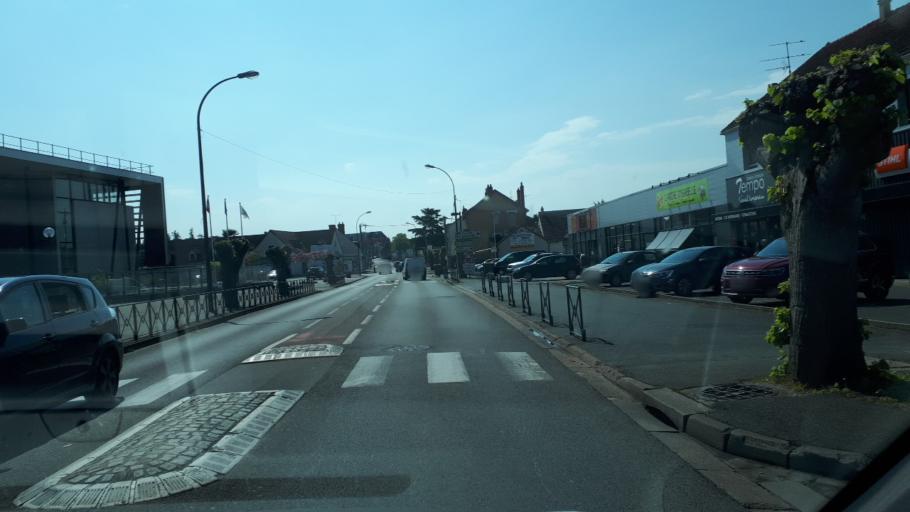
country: FR
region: Centre
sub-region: Departement du Loir-et-Cher
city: Romorantin-Lanthenay
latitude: 47.3685
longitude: 1.7391
